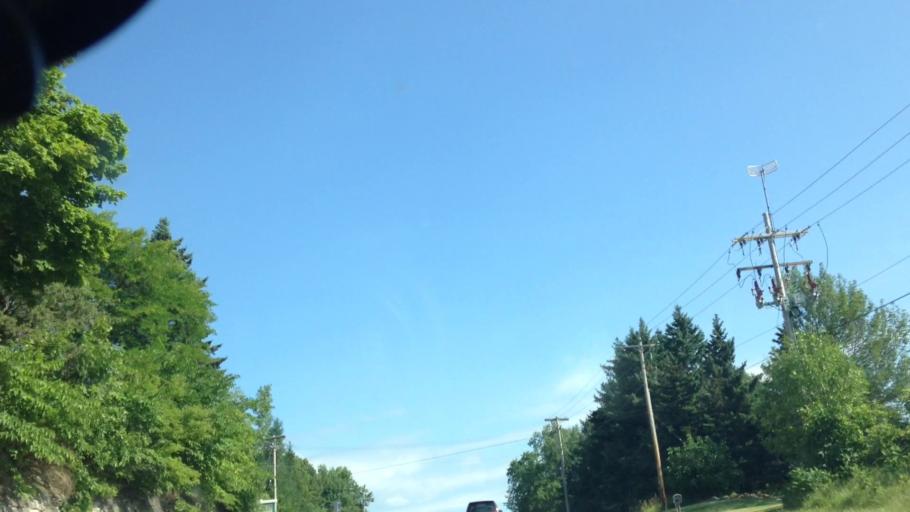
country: US
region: Wisconsin
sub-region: Washington County
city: West Bend
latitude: 43.3869
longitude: -88.2406
